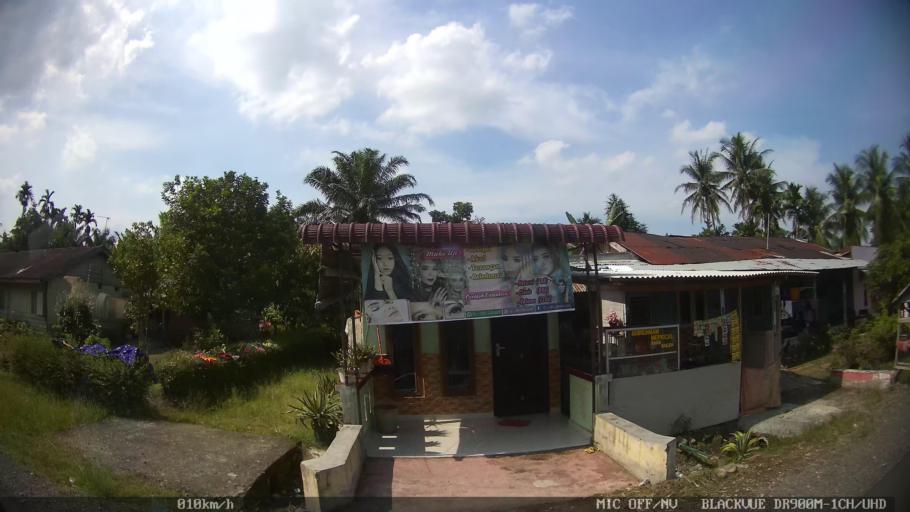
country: ID
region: North Sumatra
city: Binjai
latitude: 3.6353
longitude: 98.5203
